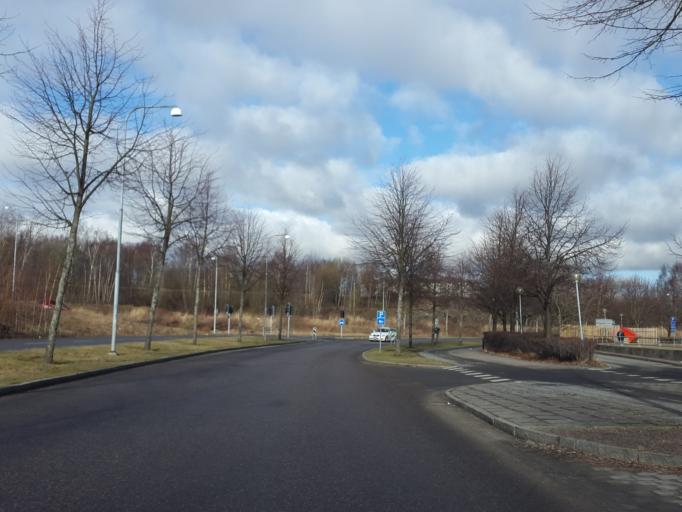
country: SE
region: Vaestra Goetaland
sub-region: Goteborg
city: Majorna
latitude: 57.7047
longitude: 11.9183
